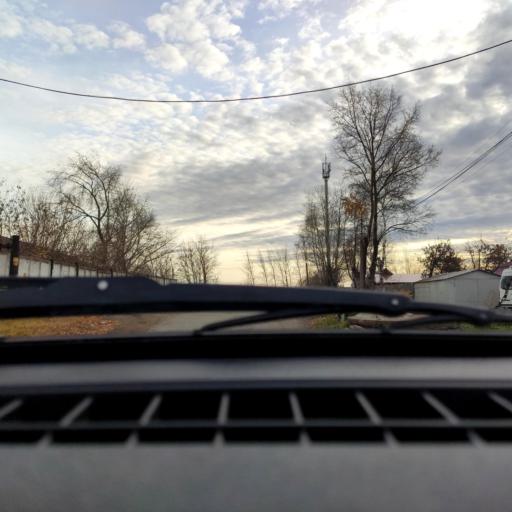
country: RU
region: Bashkortostan
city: Blagoveshchensk
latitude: 54.9005
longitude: 56.1524
